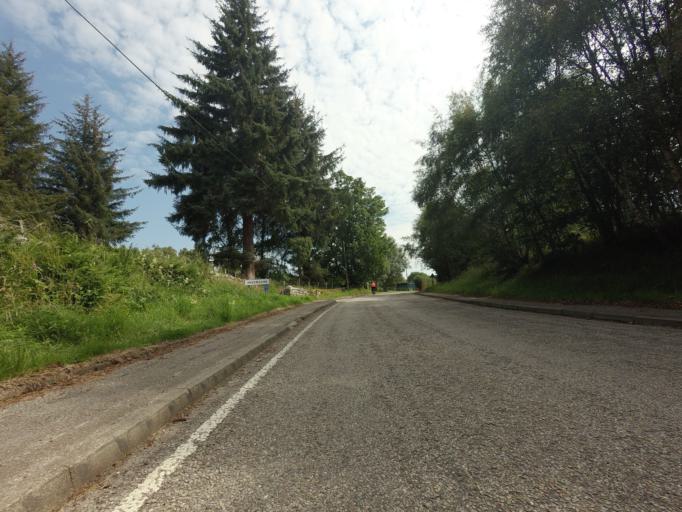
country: GB
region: Scotland
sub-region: Highland
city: Evanton
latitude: 57.9438
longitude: -4.4079
